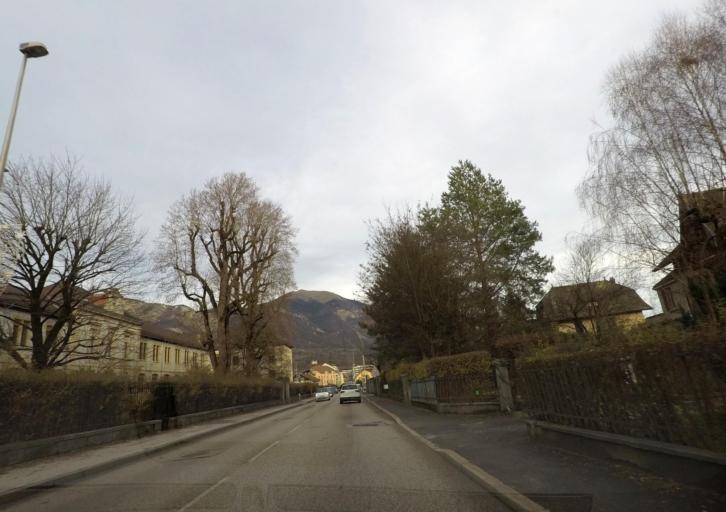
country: FR
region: Rhone-Alpes
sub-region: Departement de la Haute-Savoie
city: Bonneville
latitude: 46.0736
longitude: 6.4017
